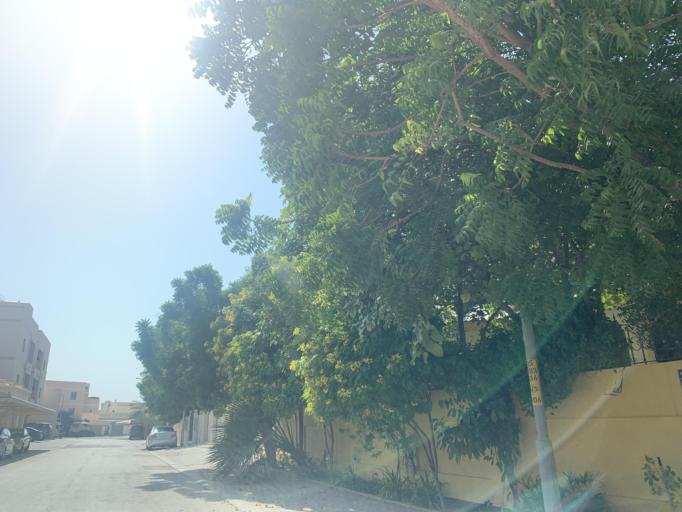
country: BH
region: Central Governorate
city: Madinat Hamad
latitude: 26.1371
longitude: 50.4954
